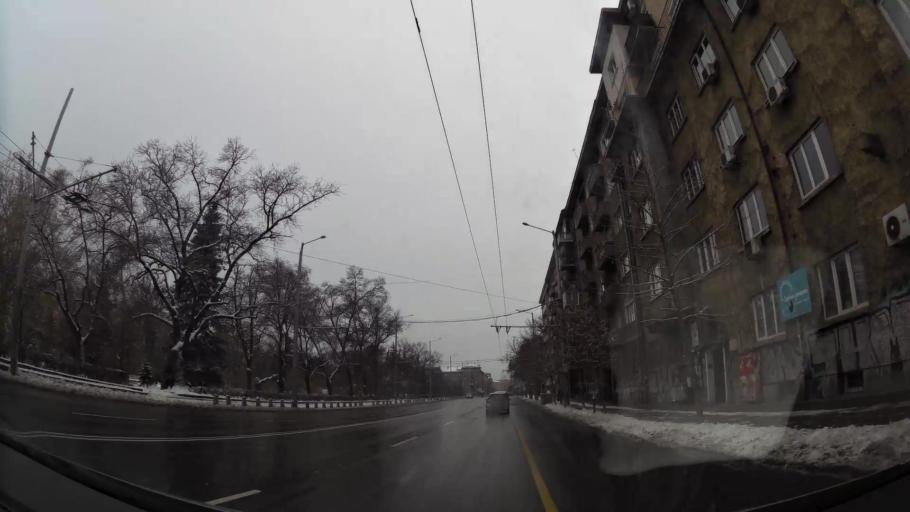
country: BG
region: Sofia-Capital
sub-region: Stolichna Obshtina
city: Sofia
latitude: 42.6922
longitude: 23.3339
